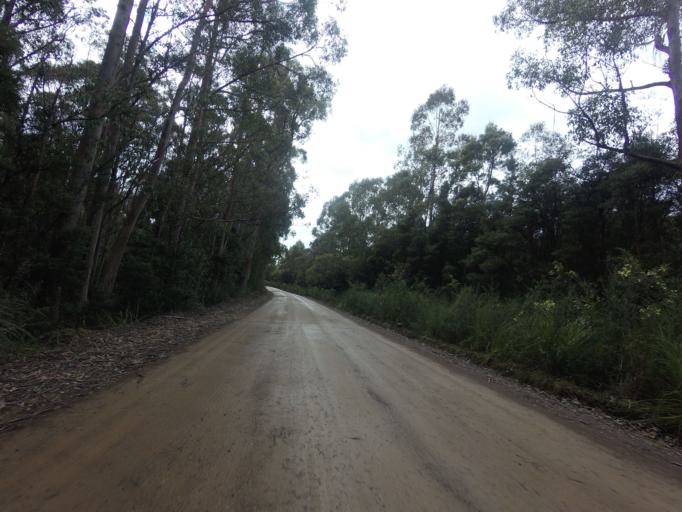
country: AU
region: Tasmania
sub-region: Huon Valley
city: Geeveston
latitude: -43.4546
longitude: 146.9044
